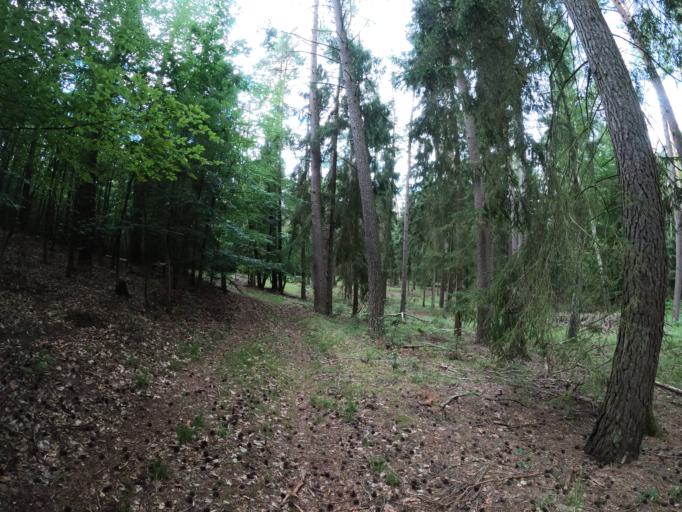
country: DE
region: Brandenburg
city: Angermunde
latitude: 53.0350
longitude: 13.9270
